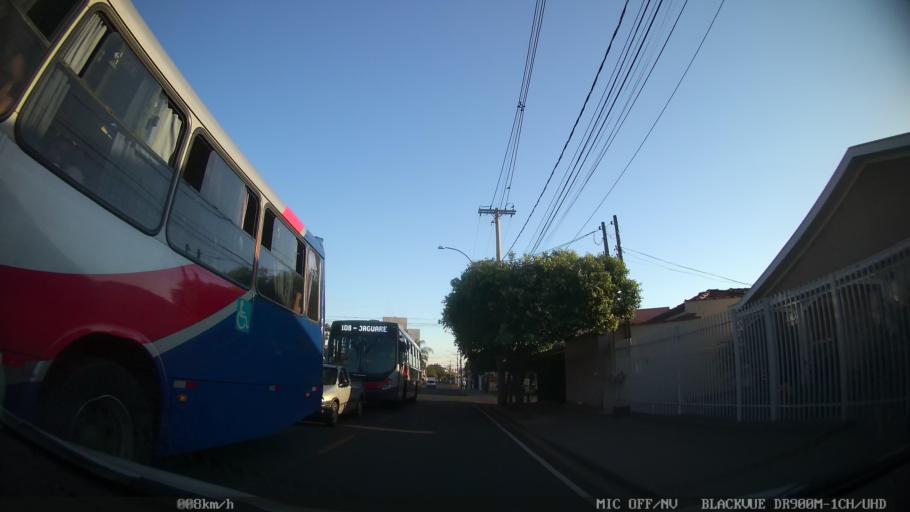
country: BR
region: Sao Paulo
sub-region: Sao Jose Do Rio Preto
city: Sao Jose do Rio Preto
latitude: -20.7975
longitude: -49.3692
